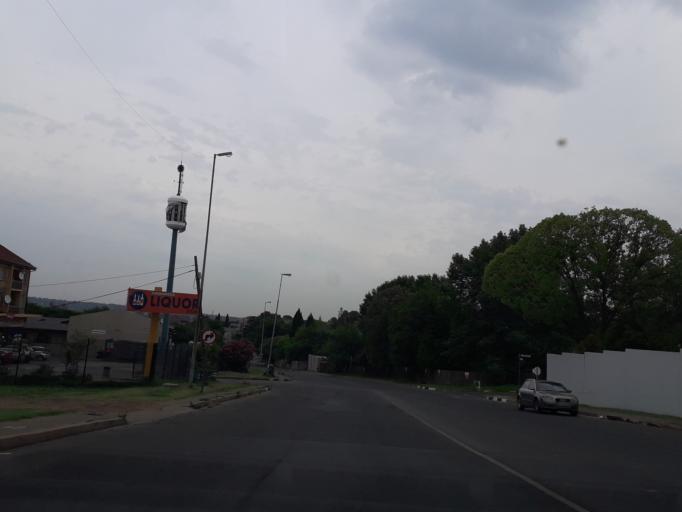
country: ZA
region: Gauteng
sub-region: City of Johannesburg Metropolitan Municipality
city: Johannesburg
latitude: -26.1305
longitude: 27.9869
